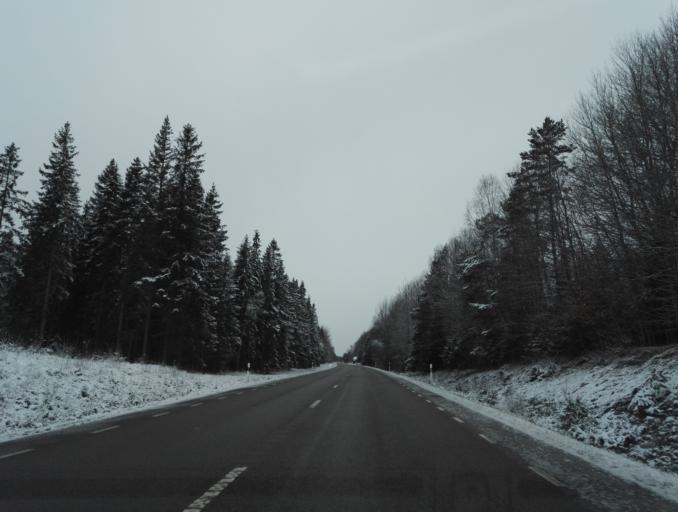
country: SE
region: Kronoberg
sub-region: Uppvidinge Kommun
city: Aseda
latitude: 57.1642
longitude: 15.3949
